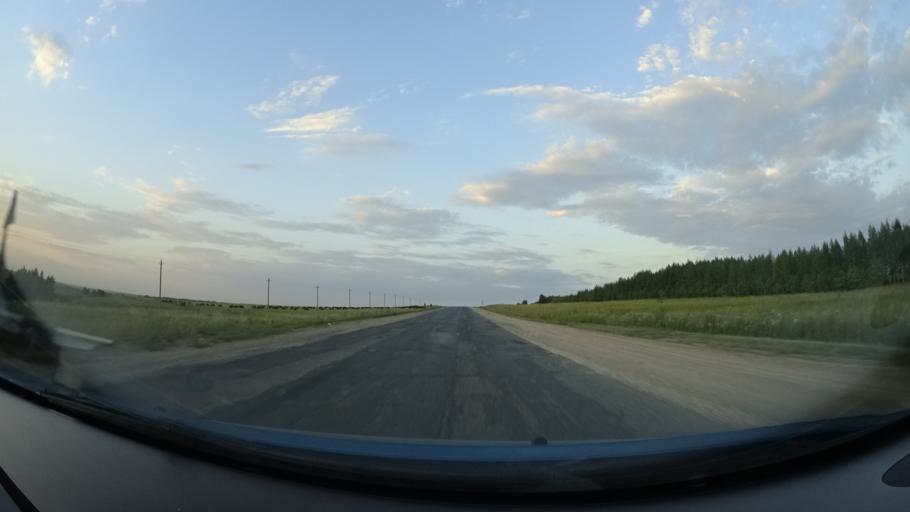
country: RU
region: Orenburg
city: Severnoye
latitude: 54.2337
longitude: 52.7760
